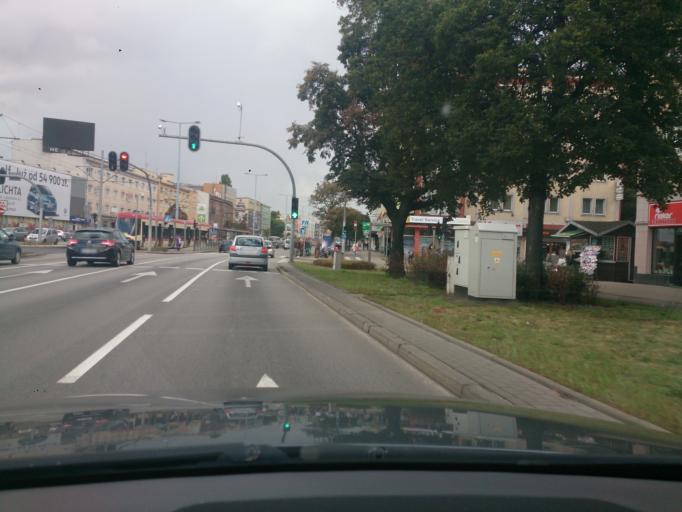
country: PL
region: Pomeranian Voivodeship
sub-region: Gdansk
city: Gdansk
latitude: 54.3780
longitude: 18.6079
